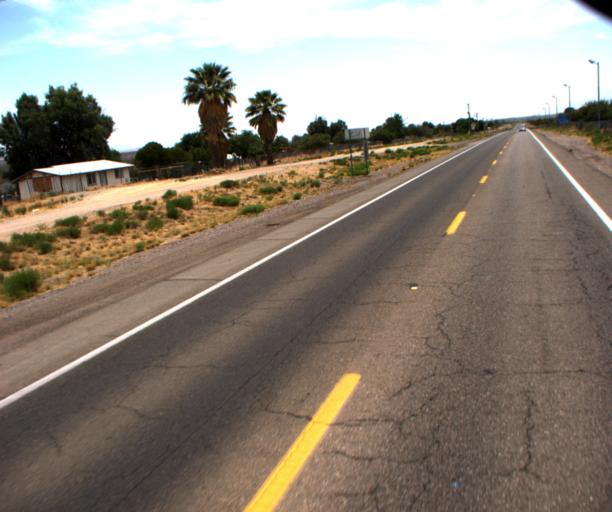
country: US
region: Arizona
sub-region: Graham County
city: Bylas
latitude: 33.1343
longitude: -110.1219
